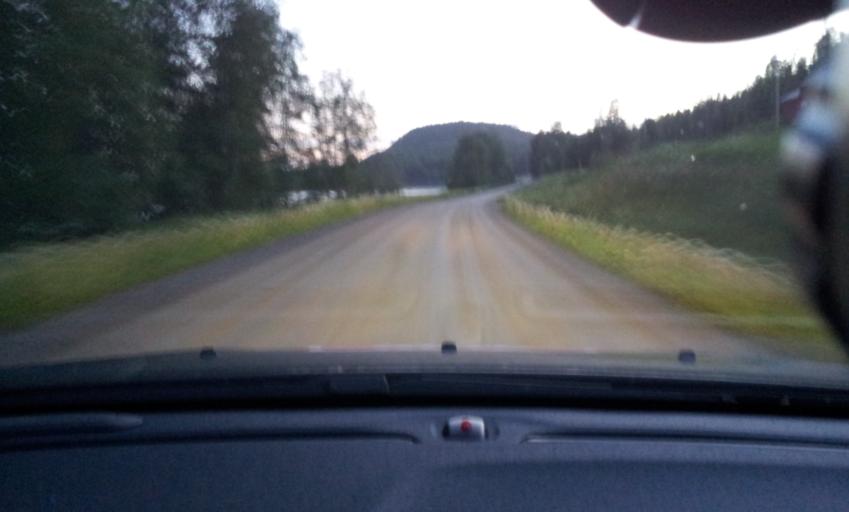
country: SE
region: Jaemtland
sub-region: Braecke Kommun
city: Braecke
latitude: 62.7174
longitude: 15.5928
